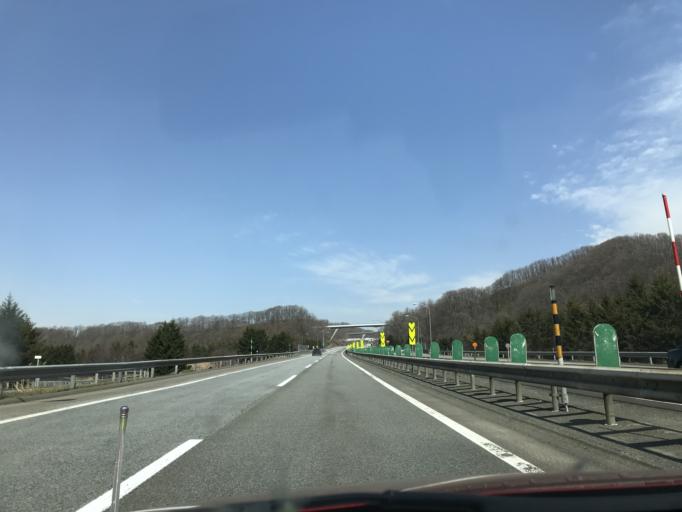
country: JP
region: Hokkaido
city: Iwamizawa
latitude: 43.2425
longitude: 141.8303
